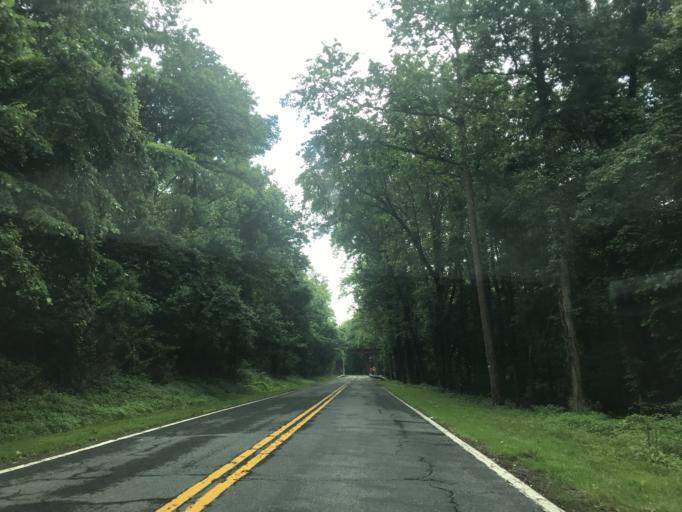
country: US
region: Maryland
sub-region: Caroline County
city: Ridgely
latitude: 38.9177
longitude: -75.9596
